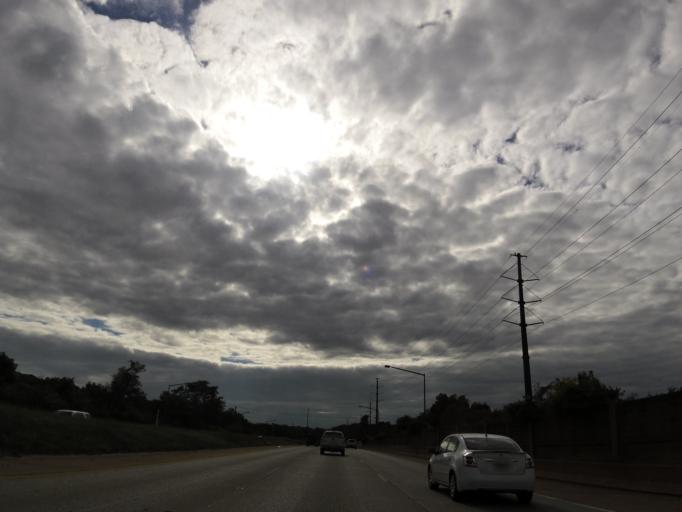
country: US
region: Tennessee
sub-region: Davidson County
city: Oak Hill
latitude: 36.1161
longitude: -86.7846
